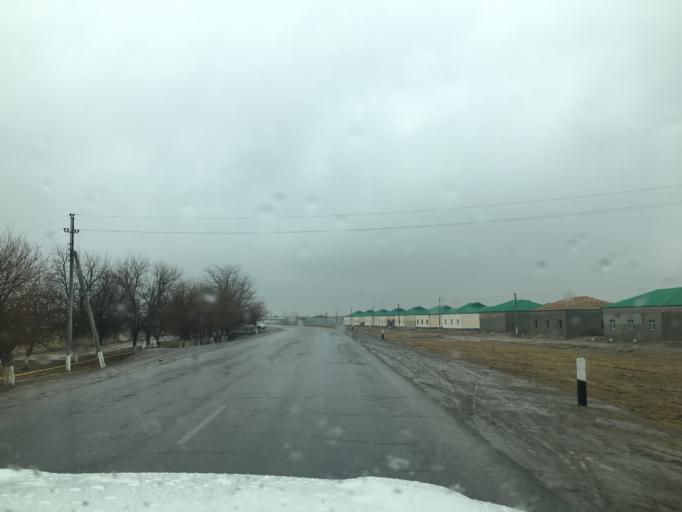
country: TM
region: Mary
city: Yoloeten
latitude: 37.2946
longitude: 62.3341
